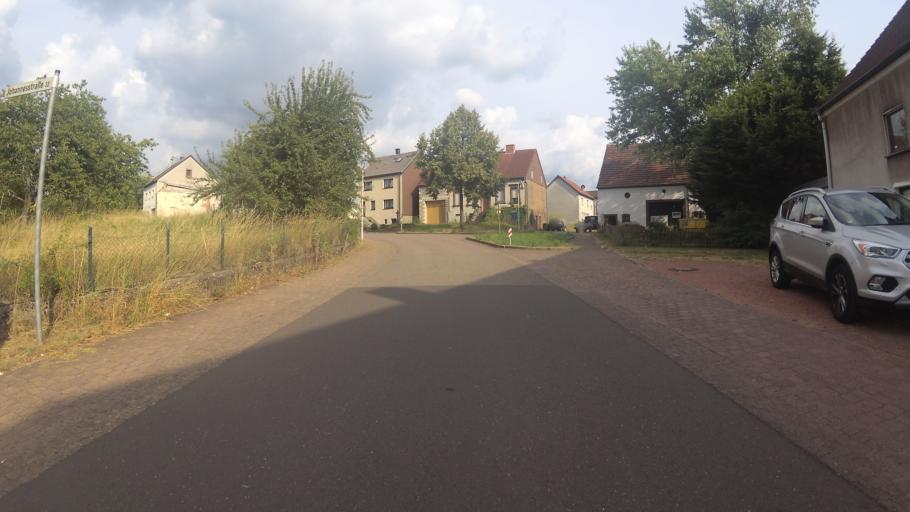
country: DE
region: Saarland
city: Illingen
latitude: 49.3730
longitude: 7.0149
